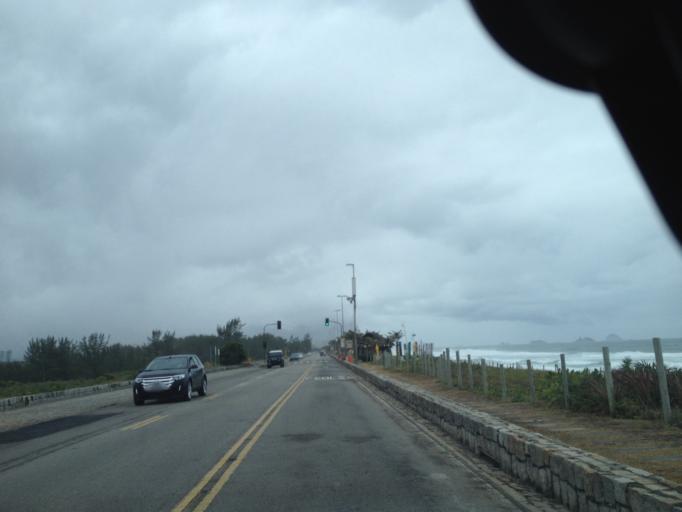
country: BR
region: Rio de Janeiro
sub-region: Nilopolis
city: Nilopolis
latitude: -23.0151
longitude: -43.4084
